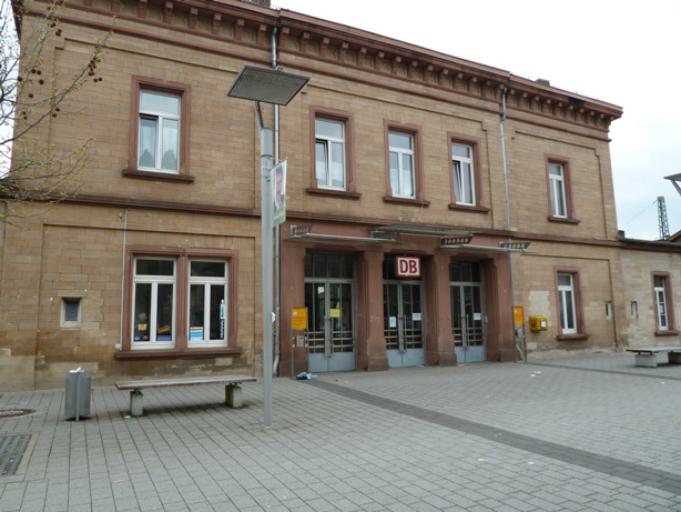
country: DE
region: Hesse
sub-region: Regierungsbezirk Darmstadt
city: Heppenheim an der Bergstrasse
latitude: 49.6412
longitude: 8.6338
